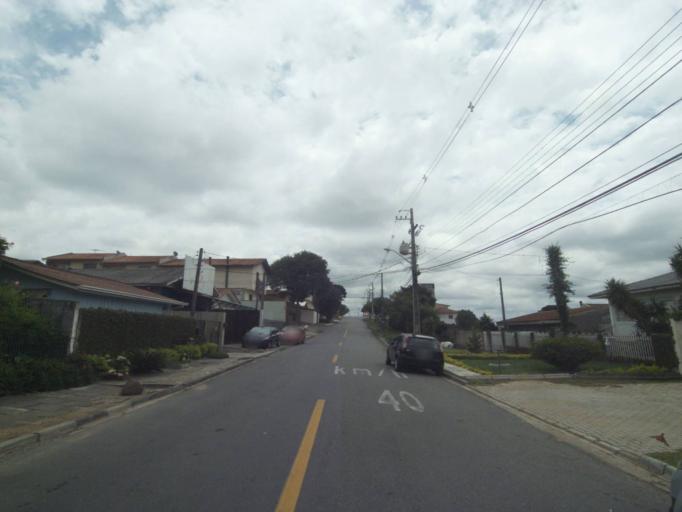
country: BR
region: Parana
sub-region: Curitiba
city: Curitiba
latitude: -25.3951
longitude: -49.2867
